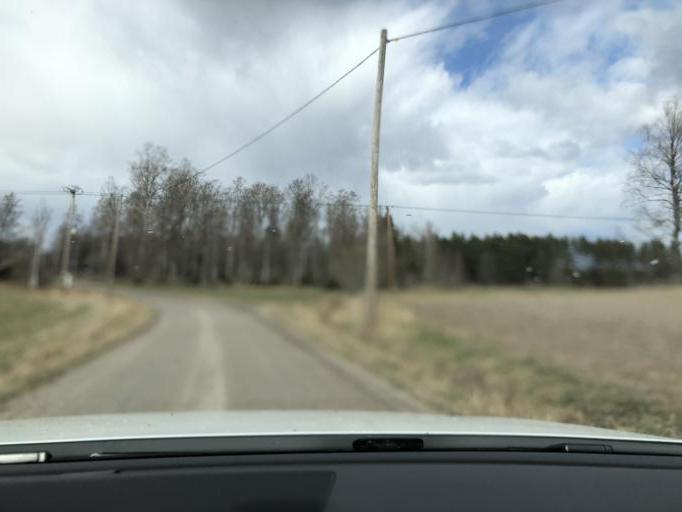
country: SE
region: Gaevleborg
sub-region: Gavle Kommun
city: Hedesunda
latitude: 60.3121
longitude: 17.1097
